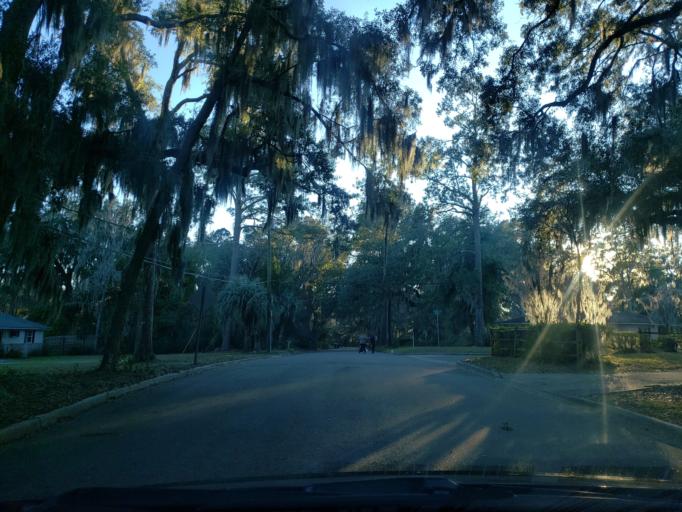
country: US
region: Georgia
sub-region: Chatham County
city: Isle of Hope
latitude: 31.9892
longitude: -81.1088
